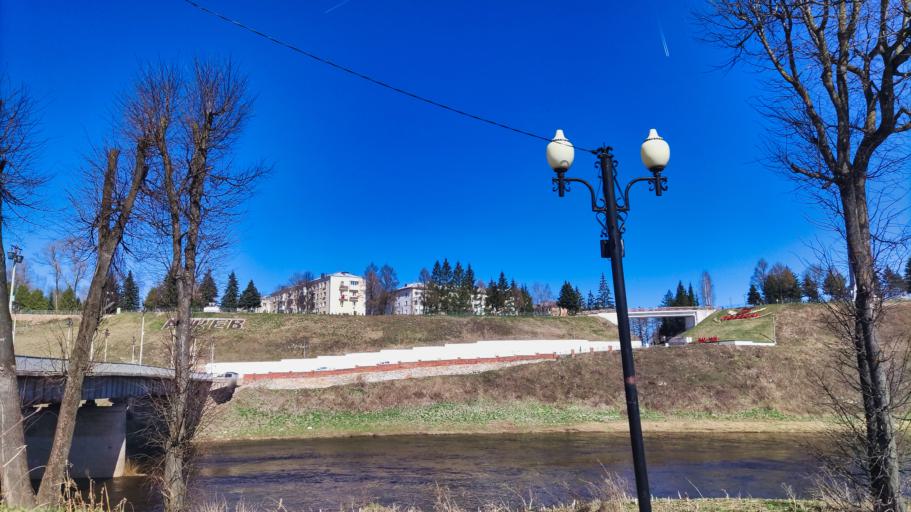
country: RU
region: Tverskaya
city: Rzhev
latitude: 56.2591
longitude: 34.3355
